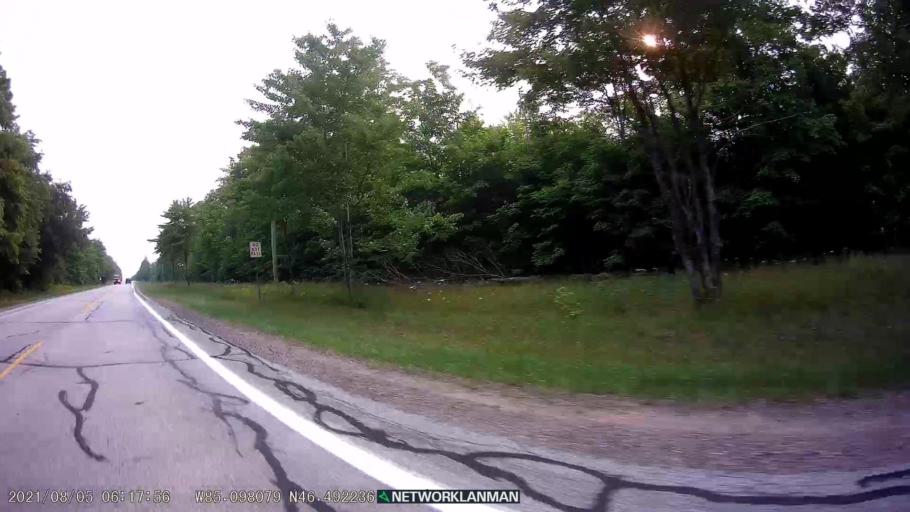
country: US
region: Michigan
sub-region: Luce County
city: Newberry
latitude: 46.4938
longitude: -85.0975
